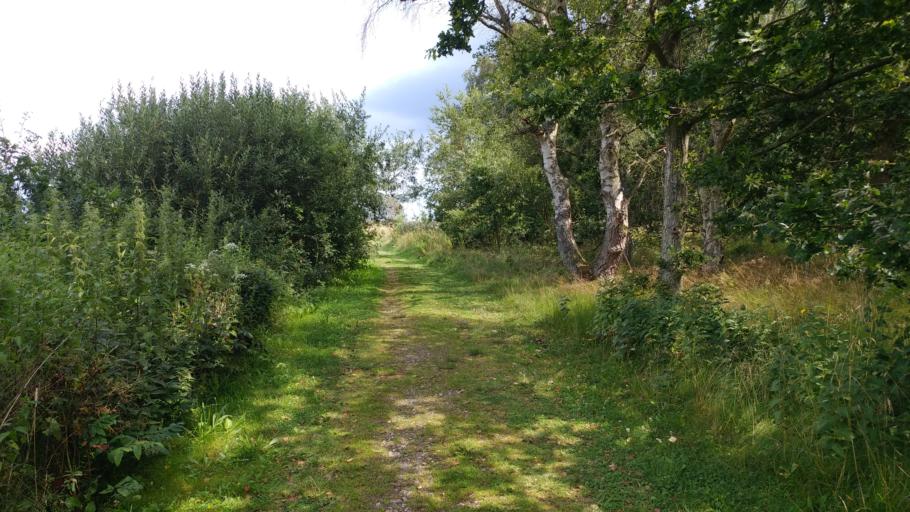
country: DK
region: Central Jutland
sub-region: Norddjurs Kommune
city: Allingabro
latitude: 56.5494
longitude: 10.3737
